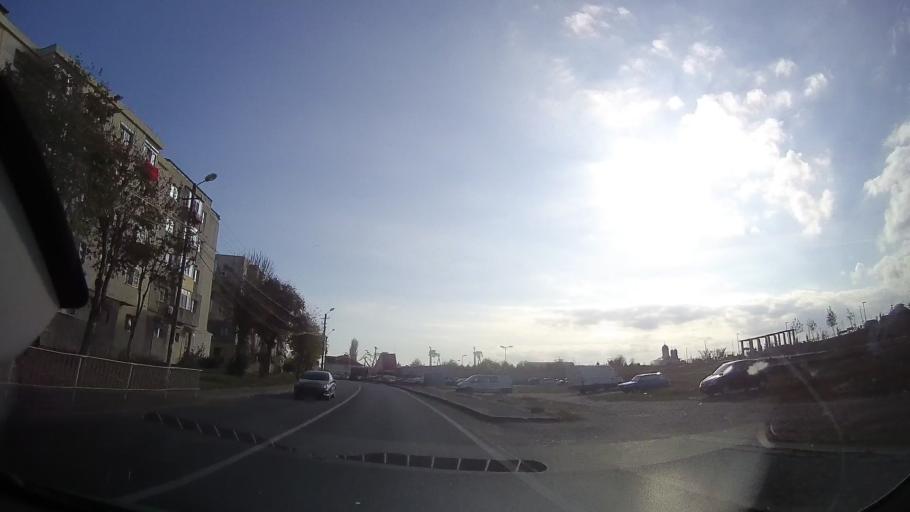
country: RO
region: Constanta
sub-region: Municipiul Mangalia
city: Mangalia
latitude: 43.8108
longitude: 28.5718
